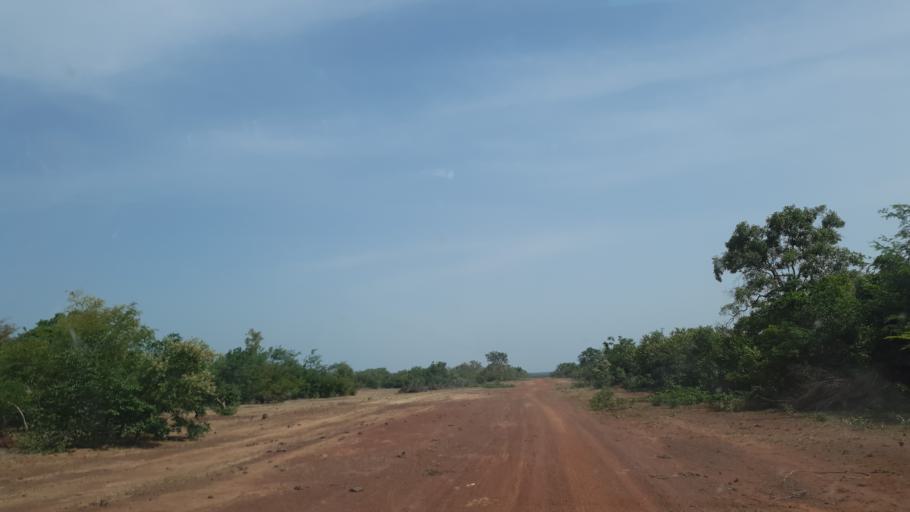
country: ML
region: Koulikoro
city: Dioila
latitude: 12.4615
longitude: -6.1916
